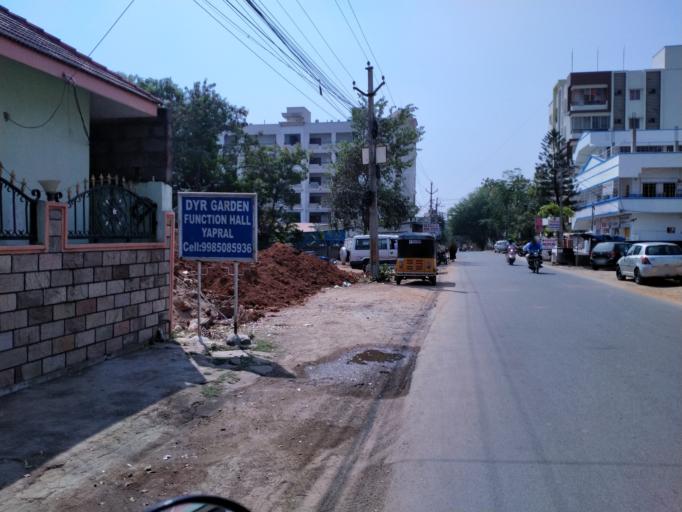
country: IN
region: Telangana
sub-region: Rangareddi
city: Secunderabad
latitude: 17.5002
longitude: 78.5468
